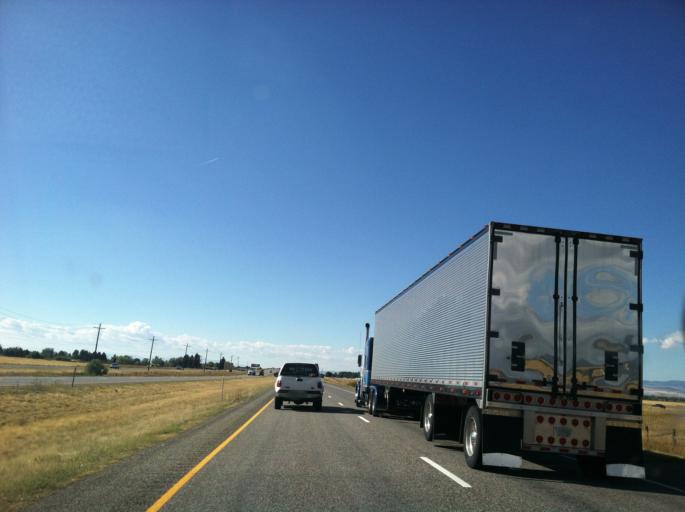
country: US
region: Montana
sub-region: Gallatin County
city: Bozeman
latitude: 45.7265
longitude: -111.0838
